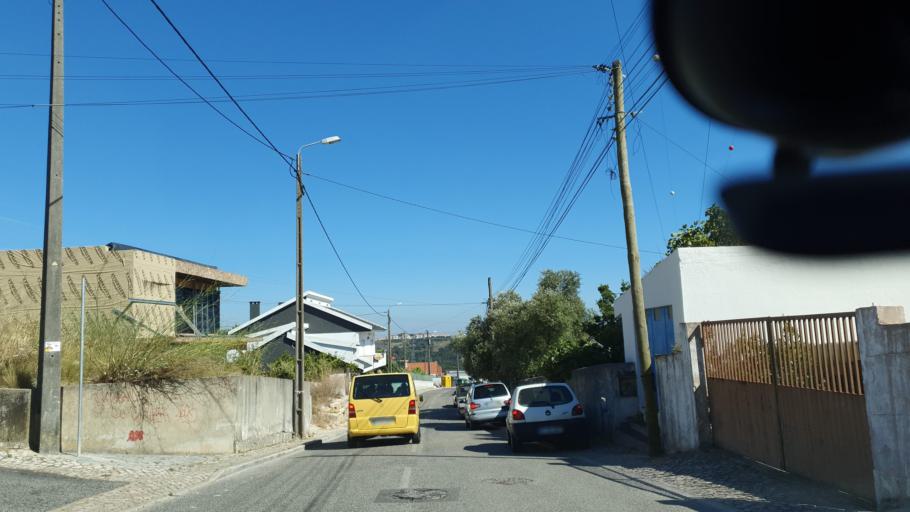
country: PT
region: Lisbon
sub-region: Sintra
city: Belas
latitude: 38.7993
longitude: -9.2507
